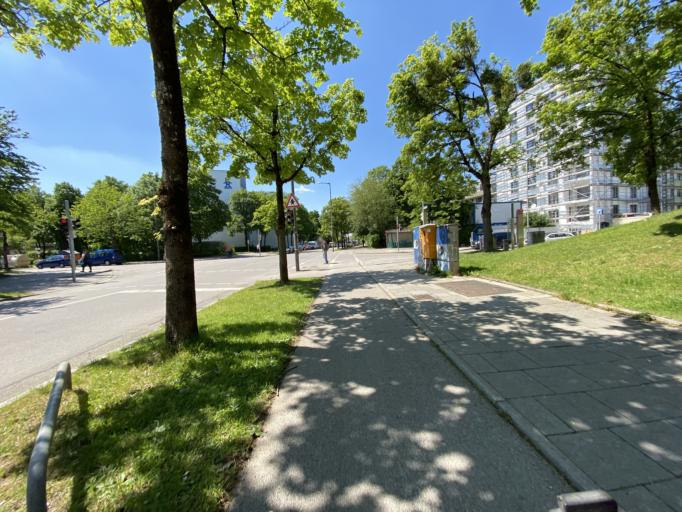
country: DE
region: Bavaria
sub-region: Upper Bavaria
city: Neuried
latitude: 48.1188
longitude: 11.4848
